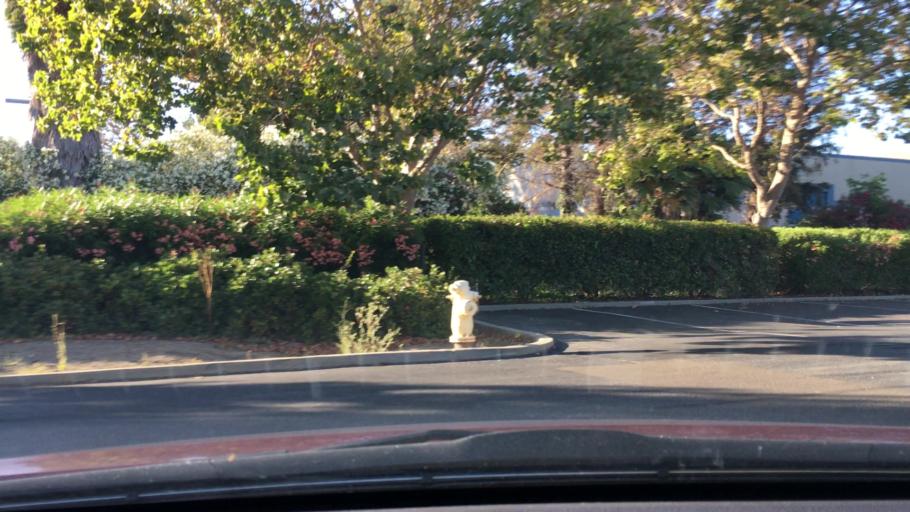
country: US
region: California
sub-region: Santa Clara County
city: Milpitas
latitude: 37.4682
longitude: -121.9195
